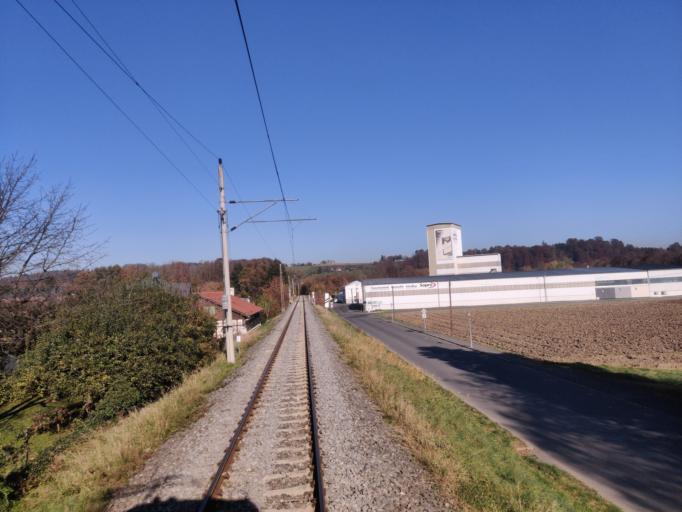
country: AT
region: Styria
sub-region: Politischer Bezirk Suedoststeiermark
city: Feldbach
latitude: 46.9531
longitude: 15.8981
